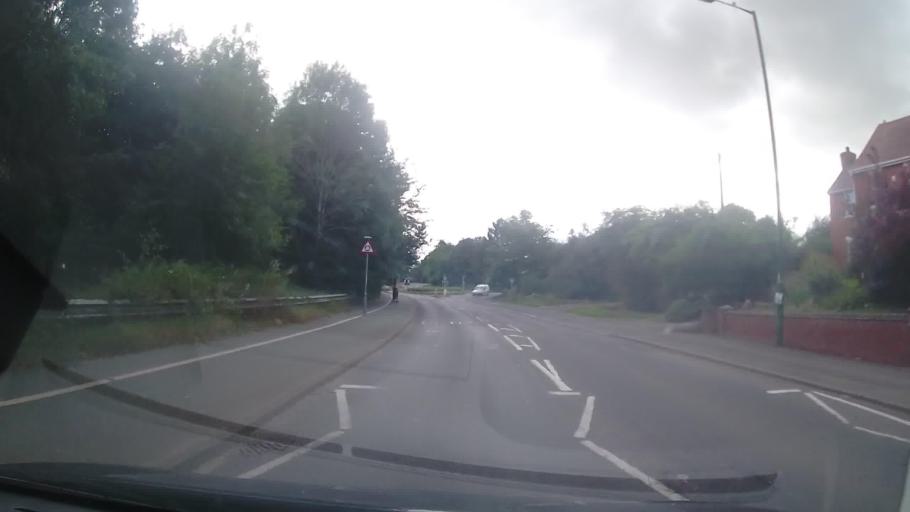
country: GB
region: England
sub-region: Shropshire
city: Bayston Hill
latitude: 52.6995
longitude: -2.7841
